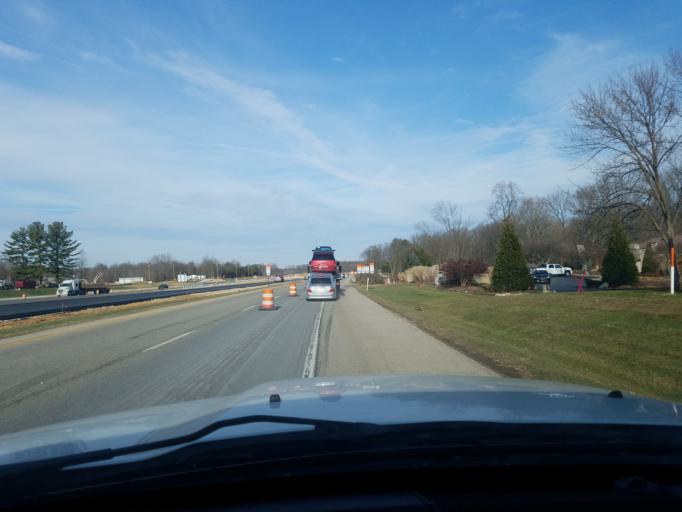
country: US
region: Indiana
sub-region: Monroe County
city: Ellettsville
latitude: 39.2821
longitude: -86.5221
